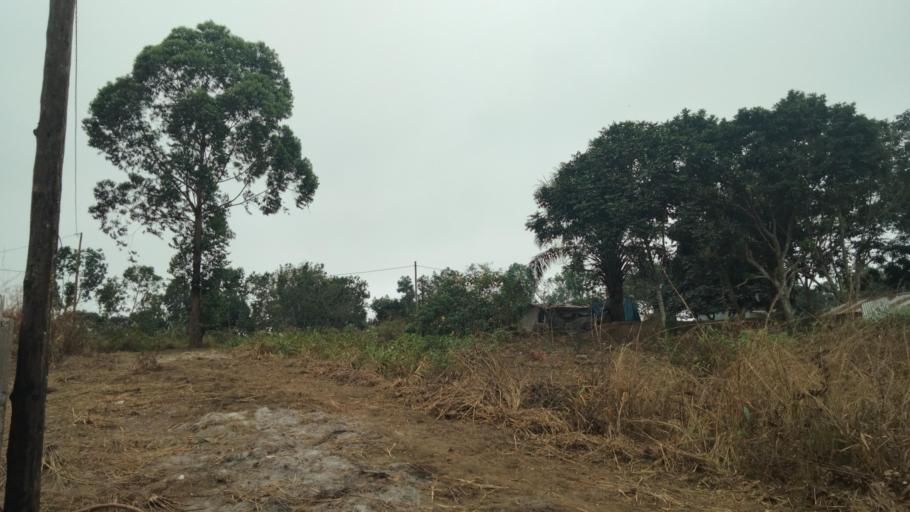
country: CG
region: Brazzaville
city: Brazzaville
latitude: -3.9817
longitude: 15.3775
